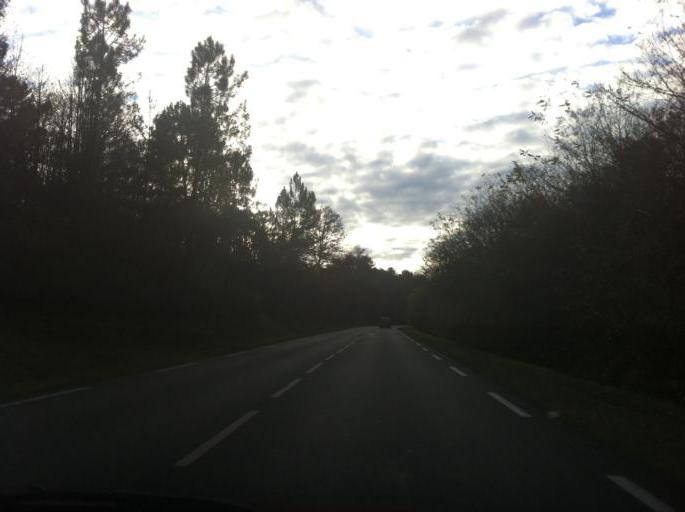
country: FR
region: Aquitaine
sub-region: Departement de la Dordogne
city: Annesse-et-Beaulieu
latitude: 45.1975
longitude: 0.6117
